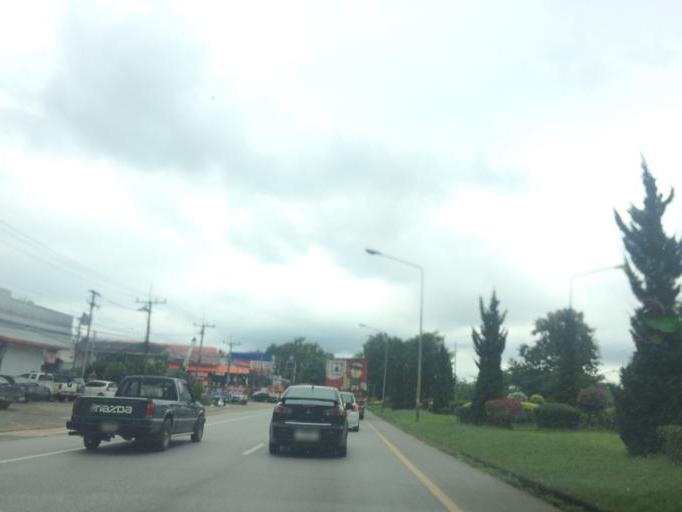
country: TH
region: Chiang Rai
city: Chiang Rai
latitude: 19.8676
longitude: 99.8241
